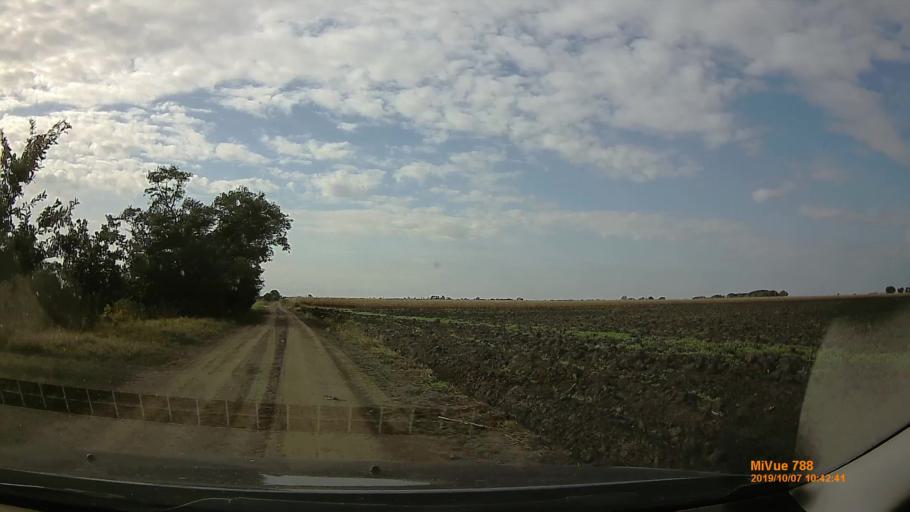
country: HU
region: Bekes
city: Kondoros
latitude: 46.7425
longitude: 20.8411
